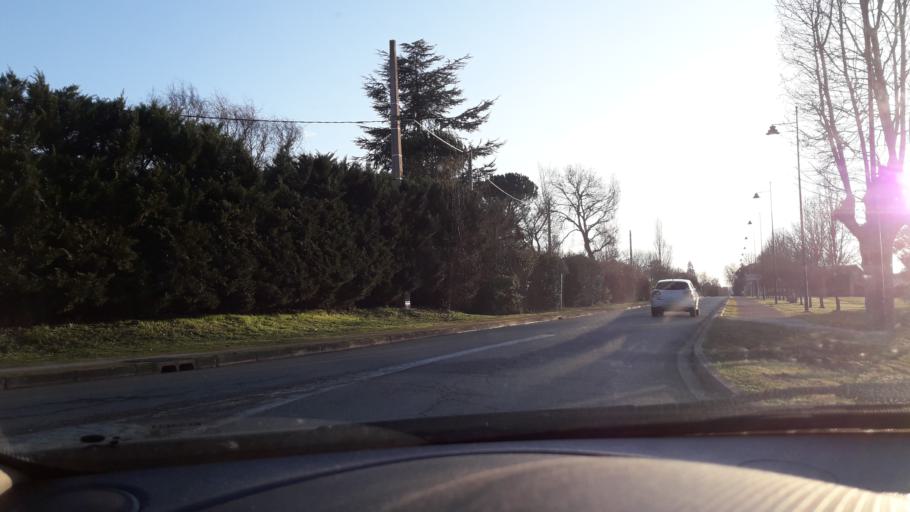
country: FR
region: Midi-Pyrenees
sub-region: Departement de la Haute-Garonne
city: Levignac
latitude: 43.6638
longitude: 1.1903
